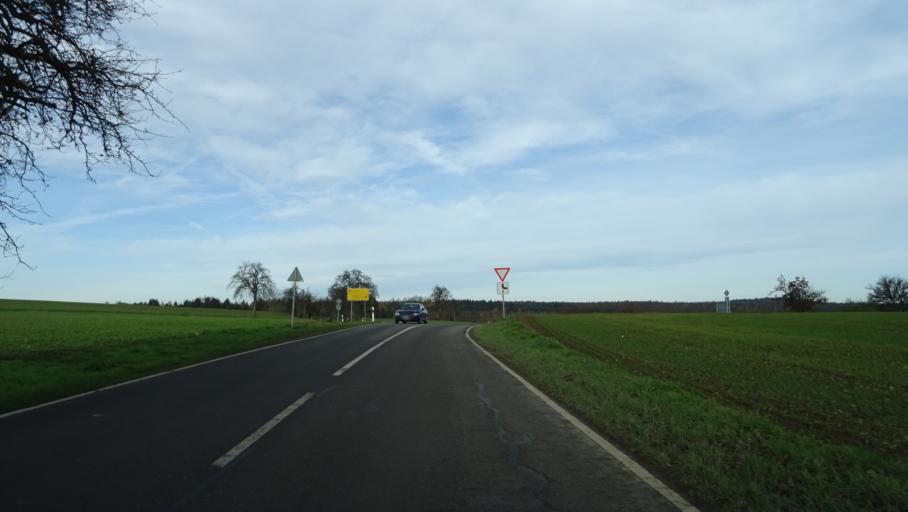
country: DE
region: Baden-Wuerttemberg
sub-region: Karlsruhe Region
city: Fahrenbach
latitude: 49.4037
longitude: 9.1207
